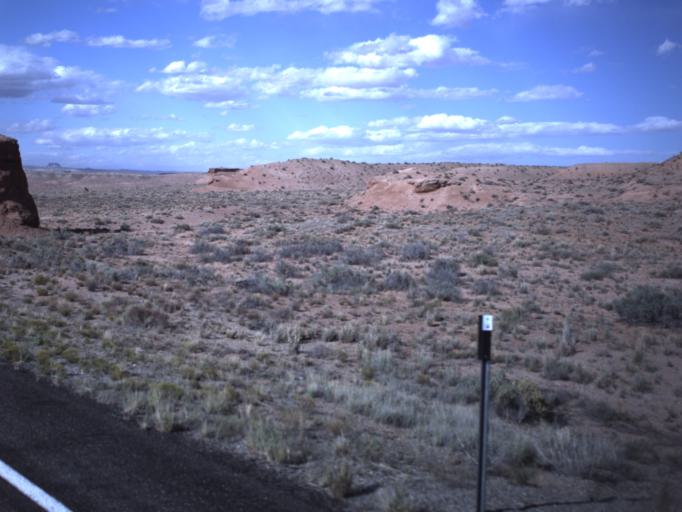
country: US
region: Utah
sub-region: Emery County
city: Ferron
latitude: 38.3554
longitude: -110.6969
